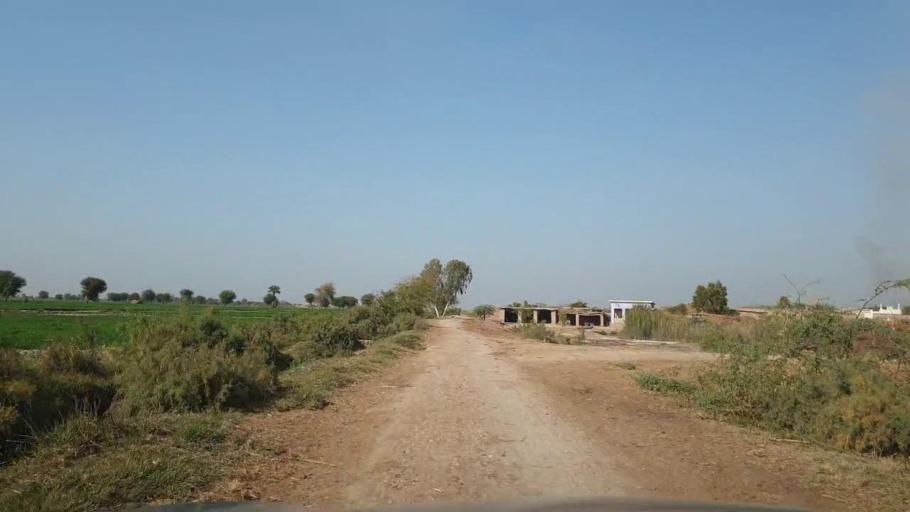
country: PK
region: Sindh
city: Berani
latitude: 25.6438
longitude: 68.8264
